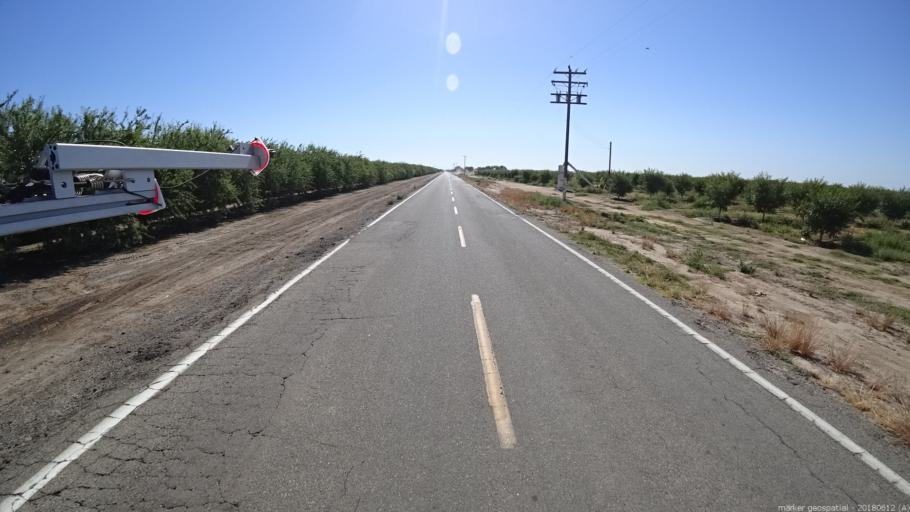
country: US
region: California
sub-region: Madera County
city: Chowchilla
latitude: 37.0181
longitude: -120.3906
